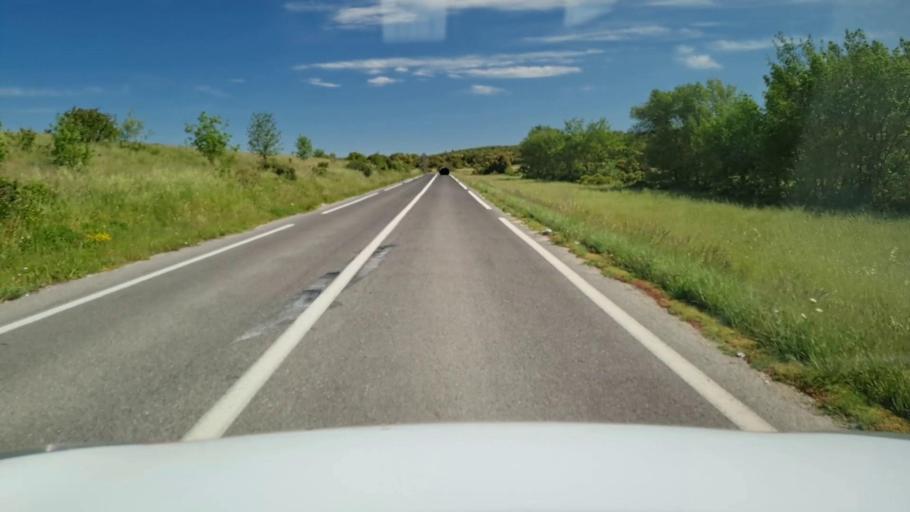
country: FR
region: Languedoc-Roussillon
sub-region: Departement du Gard
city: Villevieille
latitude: 43.8615
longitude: 4.0984
